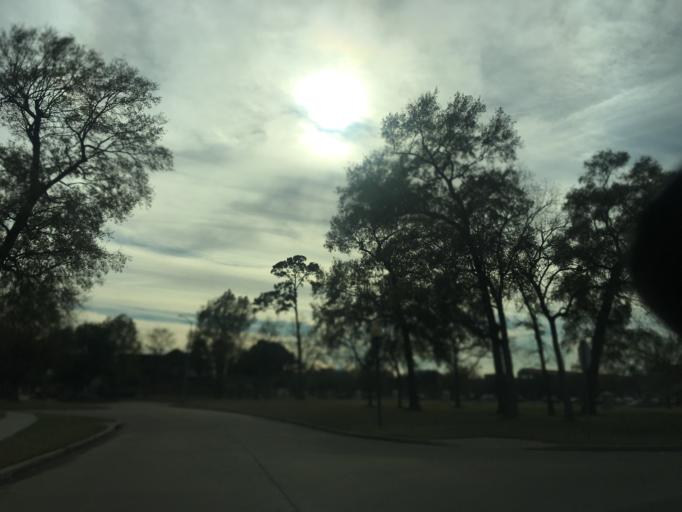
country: US
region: Texas
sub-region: Harris County
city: Cloverleaf
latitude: 29.8125
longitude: -95.1713
